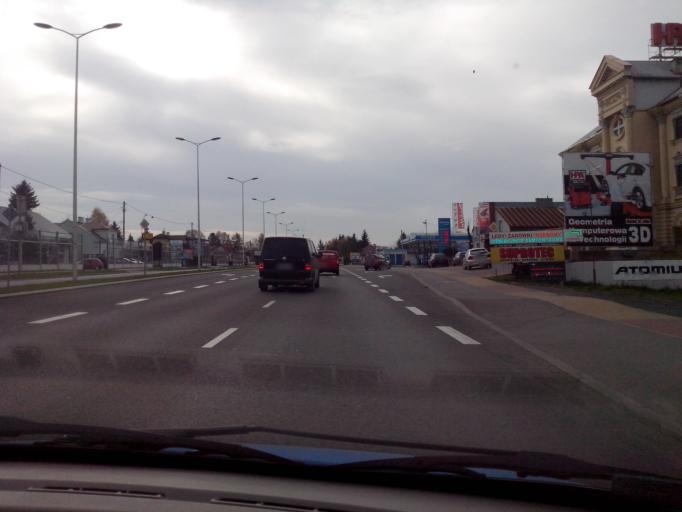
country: PL
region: Subcarpathian Voivodeship
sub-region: Powiat rzeszowski
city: Boguchwala
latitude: 50.0136
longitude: 21.9703
